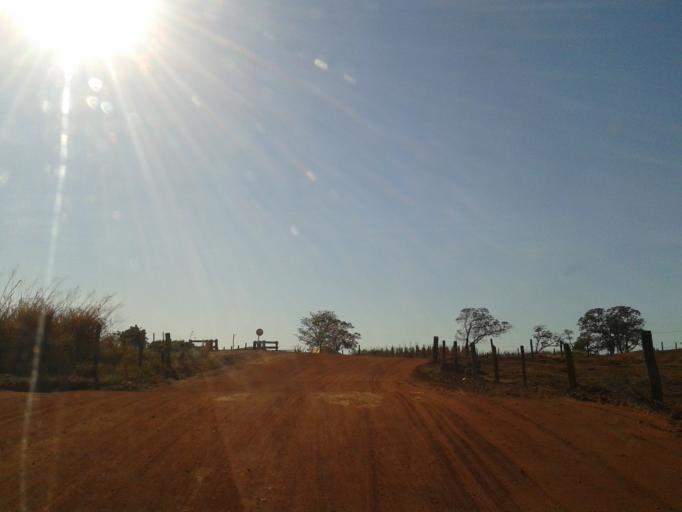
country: BR
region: Minas Gerais
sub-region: Ituiutaba
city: Ituiutaba
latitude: -18.9757
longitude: -49.4128
